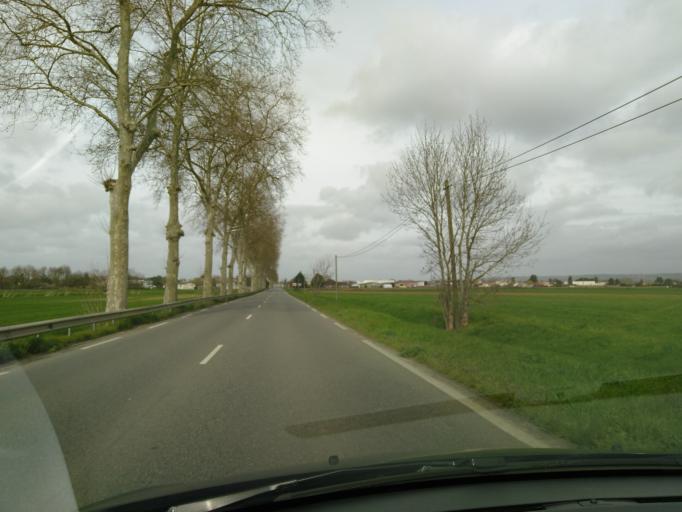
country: FR
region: Midi-Pyrenees
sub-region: Departement de la Haute-Garonne
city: Merville
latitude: 43.7497
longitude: 1.3055
